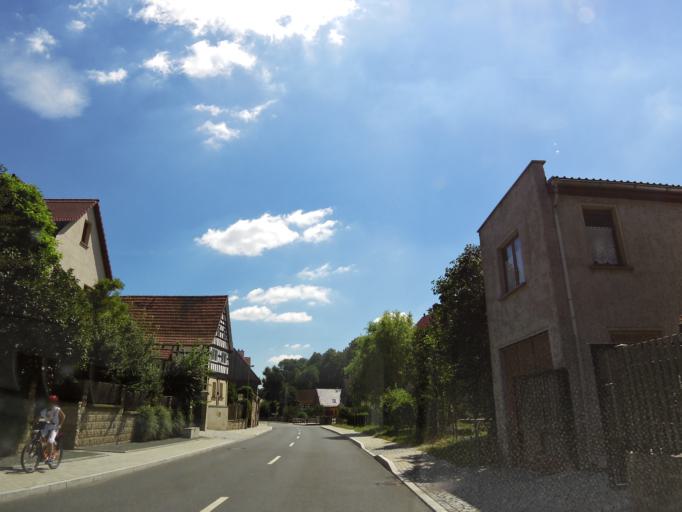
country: DE
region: Thuringia
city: Kraftsdorf
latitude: 50.8778
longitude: 11.9060
